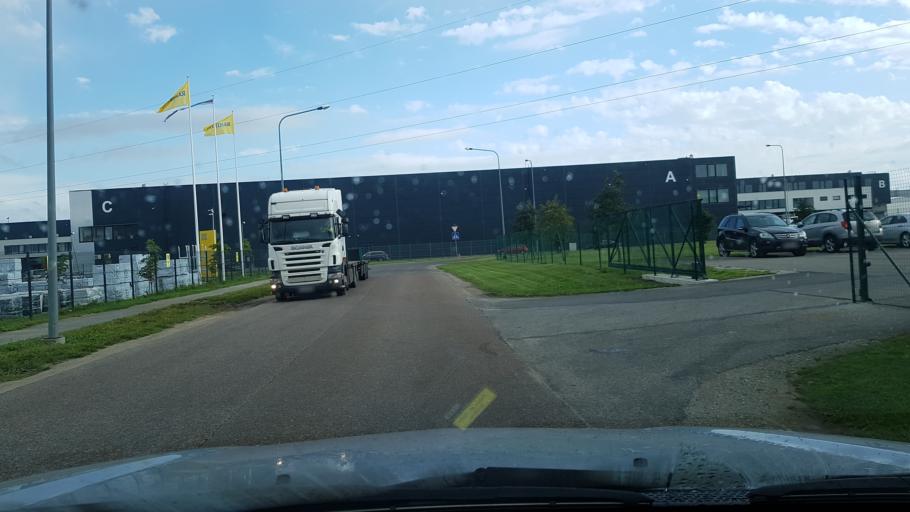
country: EE
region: Harju
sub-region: Rae vald
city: Jueri
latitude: 59.3625
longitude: 24.8824
